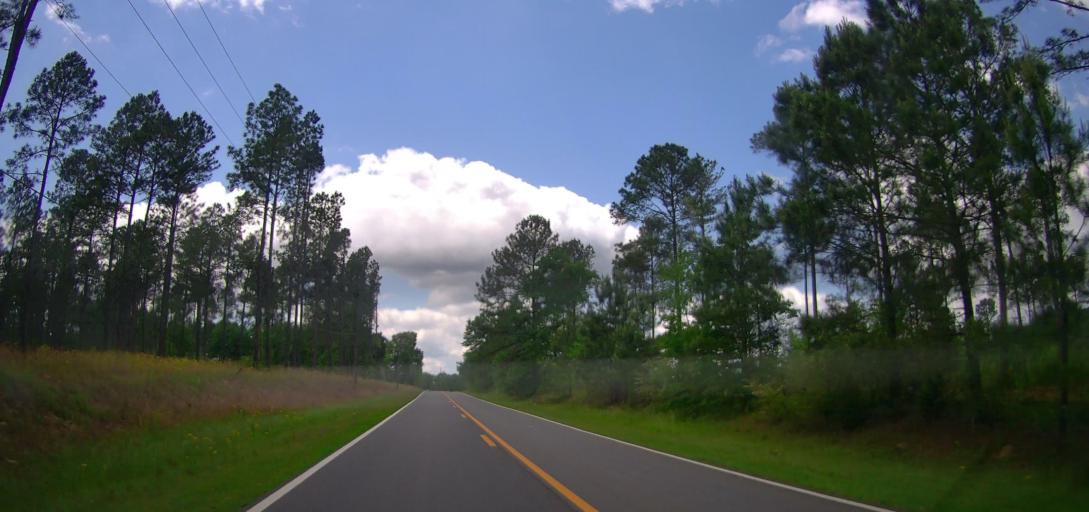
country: US
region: Georgia
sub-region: Laurens County
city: Dublin
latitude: 32.6014
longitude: -82.9212
